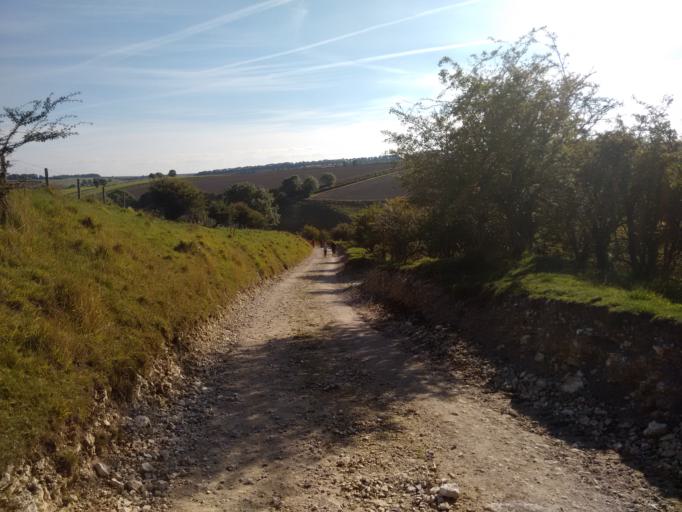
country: GB
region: England
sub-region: North Yorkshire
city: Thixendale
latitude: 54.0419
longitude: -0.7216
